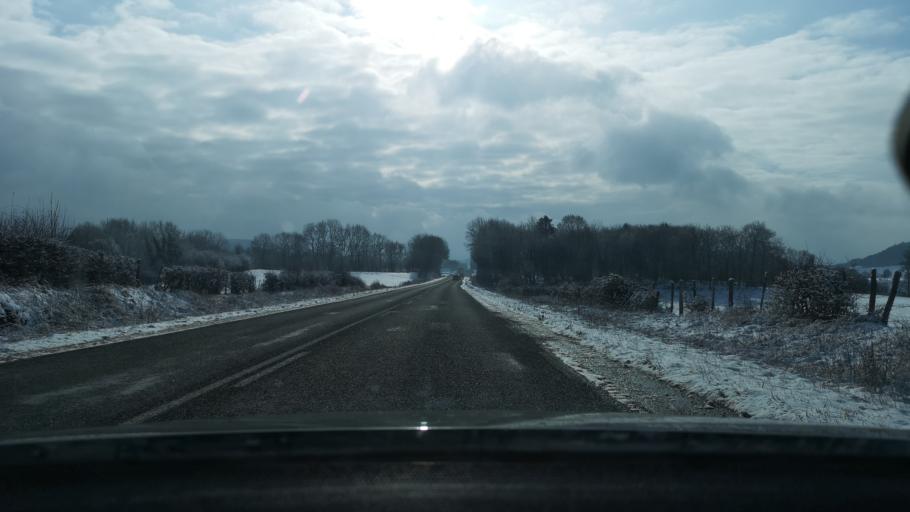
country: FR
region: Franche-Comte
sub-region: Departement du Jura
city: Orgelet
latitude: 46.5650
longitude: 5.5949
